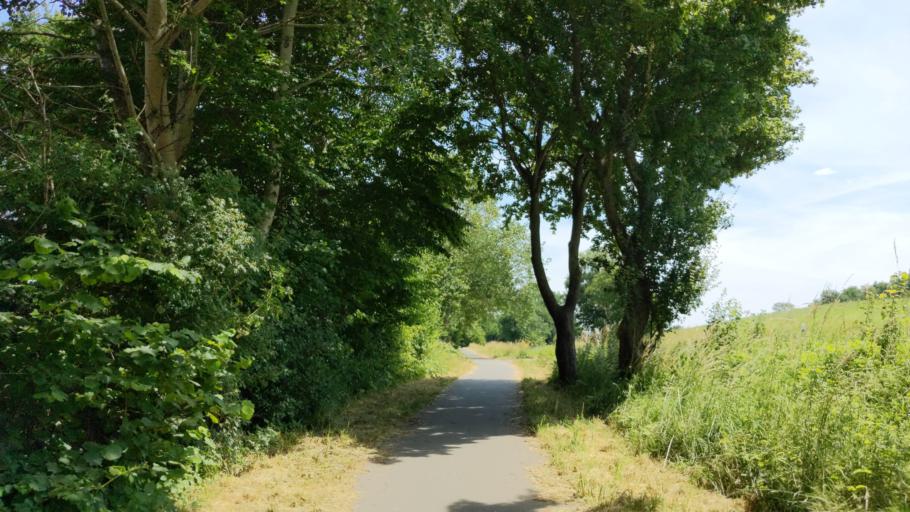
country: DE
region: Schleswig-Holstein
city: Bosdorf
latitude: 54.1488
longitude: 10.5077
